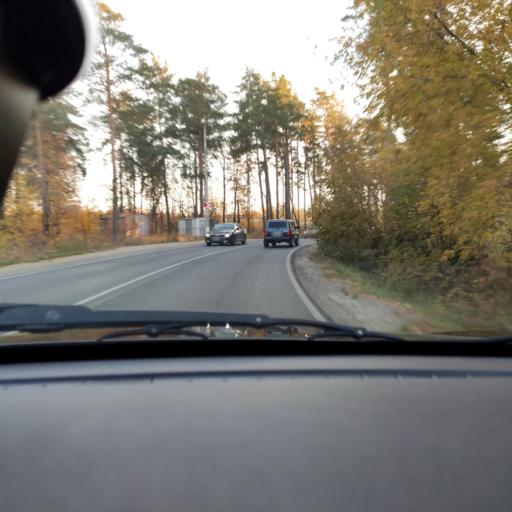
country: RU
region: Samara
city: Tol'yatti
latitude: 53.4883
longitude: 49.3102
